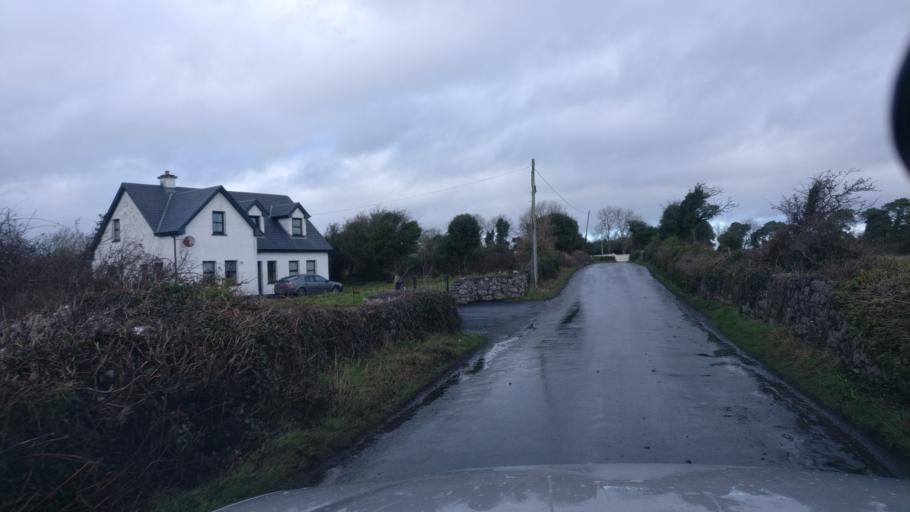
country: IE
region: Connaught
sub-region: County Galway
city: Loughrea
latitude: 53.2521
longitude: -8.6495
